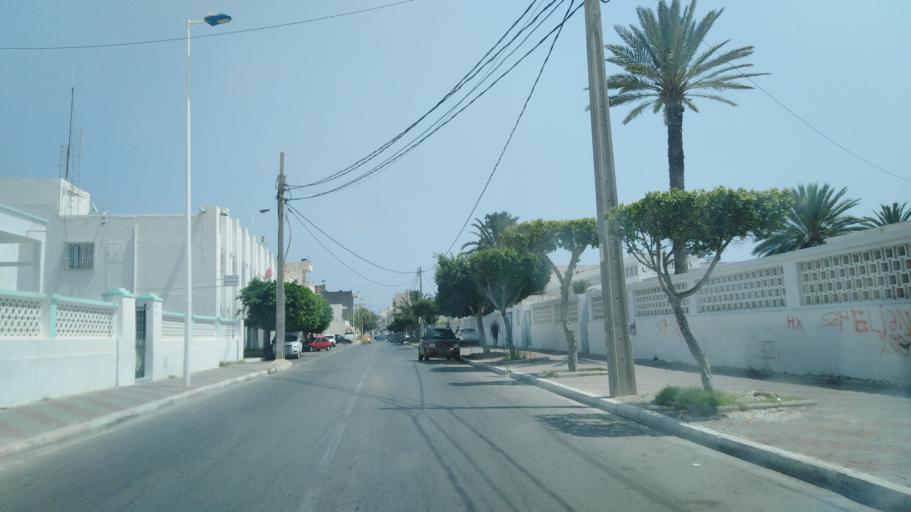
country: TN
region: Al Mahdiyah
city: Mahdia
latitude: 35.5111
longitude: 11.0487
